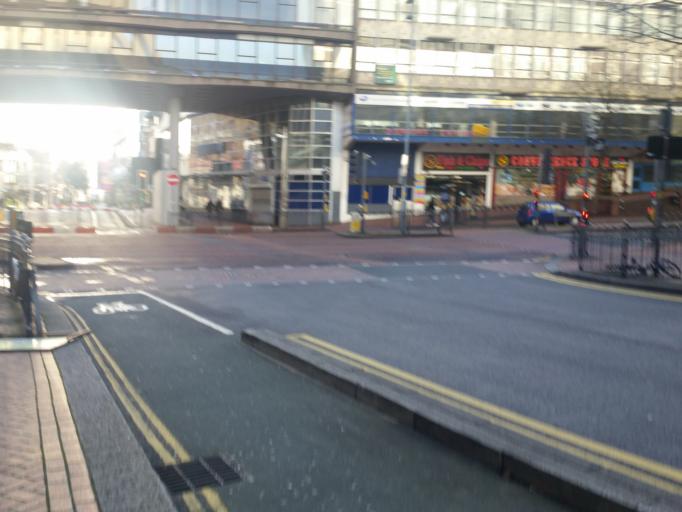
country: GB
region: England
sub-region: City and Borough of Birmingham
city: Birmingham
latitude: 52.4758
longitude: -1.8989
